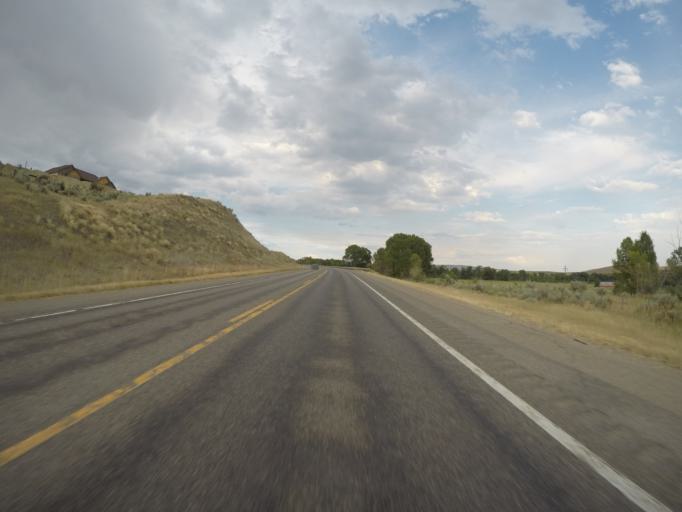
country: US
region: Colorado
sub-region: Moffat County
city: Craig
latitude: 40.5235
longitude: -107.4660
